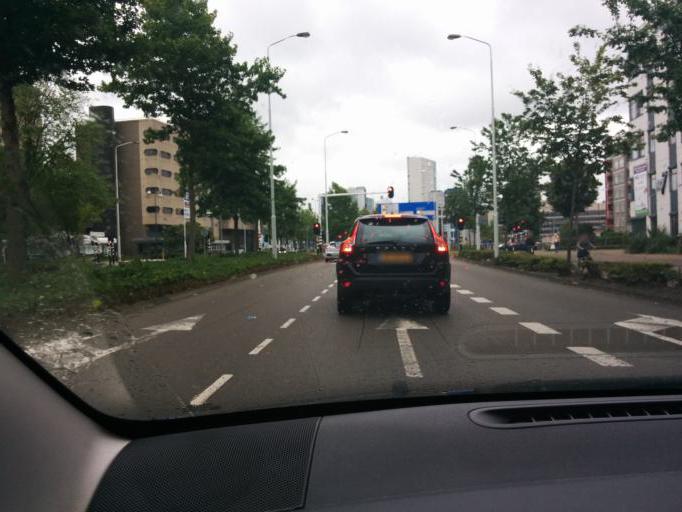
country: NL
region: North Brabant
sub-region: Gemeente Eindhoven
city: Eindhoven
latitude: 51.4450
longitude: 5.4712
